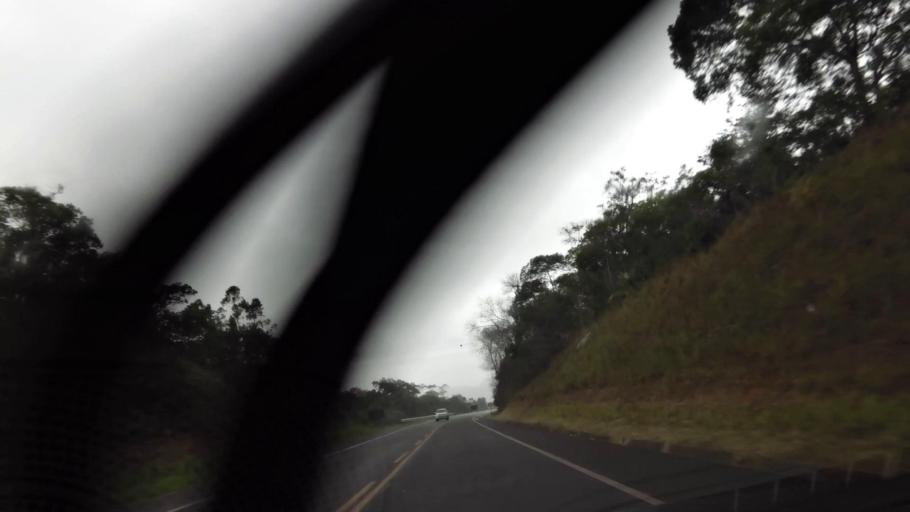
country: BR
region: Espirito Santo
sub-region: Guarapari
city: Guarapari
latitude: -20.6360
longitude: -40.5272
